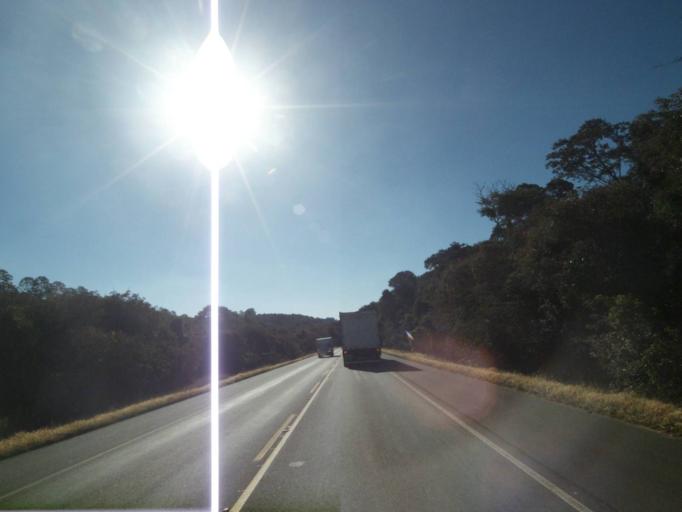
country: BR
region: Parana
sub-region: Tibagi
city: Tibagi
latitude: -24.5560
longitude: -50.4559
